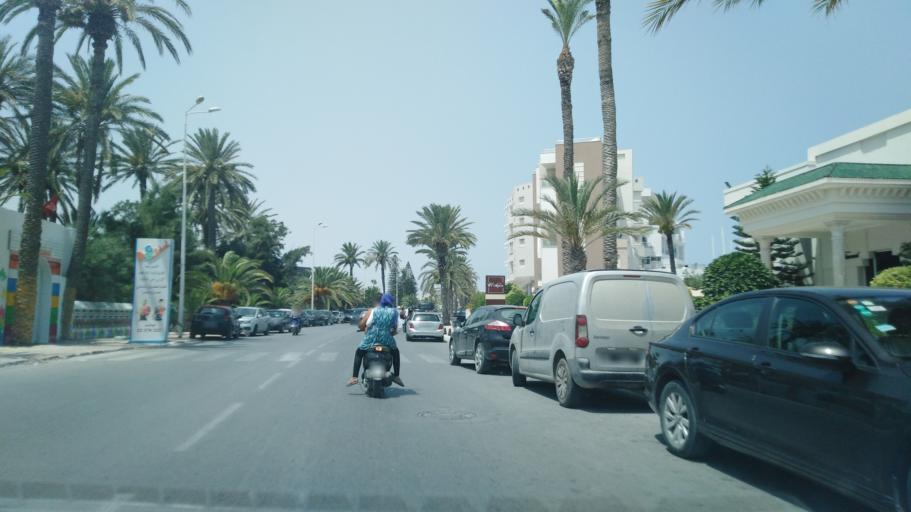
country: TN
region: Al Mahdiyah
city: Mahdia
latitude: 35.5130
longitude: 11.0482
